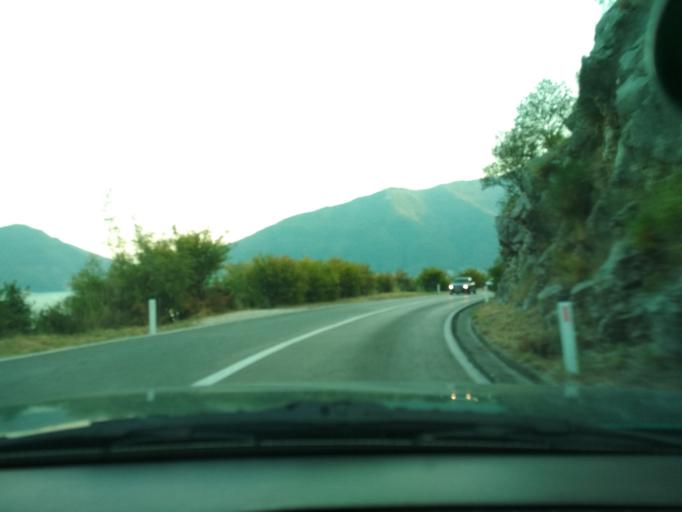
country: ME
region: Kotor
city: Risan
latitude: 42.5094
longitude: 18.6787
